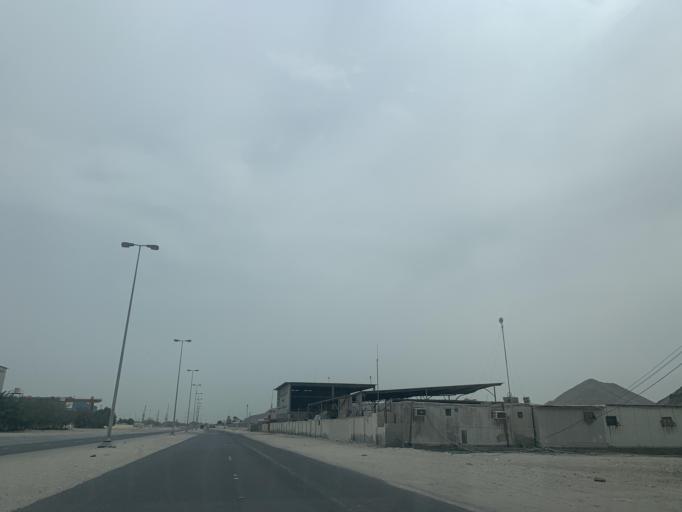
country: BH
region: Muharraq
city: Al Hadd
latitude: 26.2087
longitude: 50.6589
